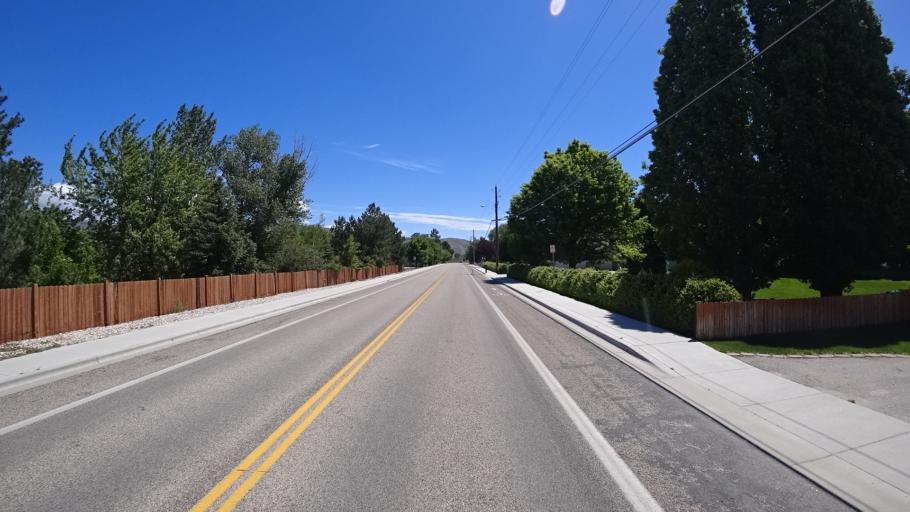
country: US
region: Idaho
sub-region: Ada County
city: Boise
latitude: 43.5641
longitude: -116.1377
